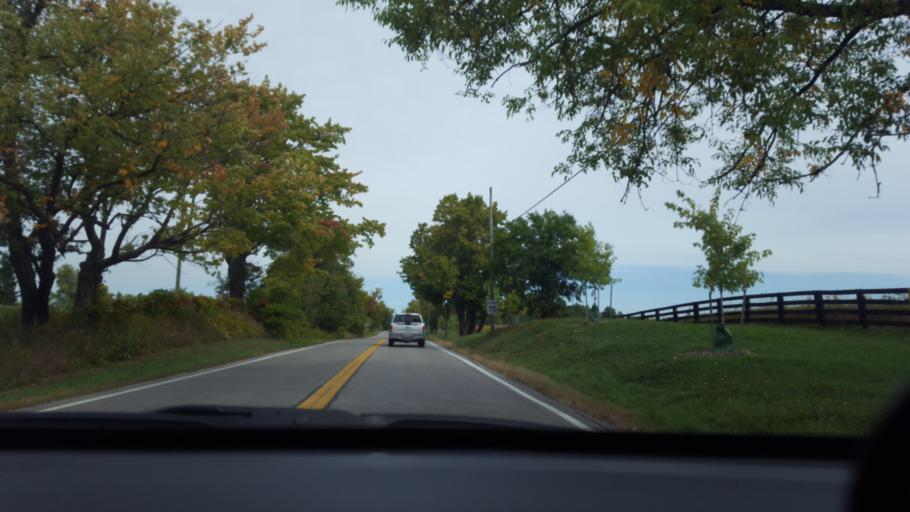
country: CA
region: Ontario
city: Newmarket
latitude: 43.9651
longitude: -79.5383
